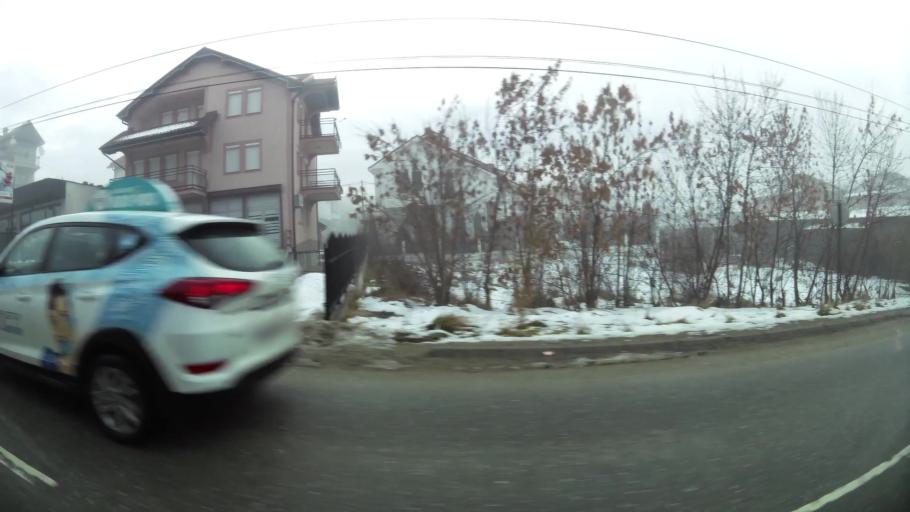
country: XK
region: Pristina
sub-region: Komuna e Prishtines
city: Pristina
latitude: 42.6612
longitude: 21.1423
